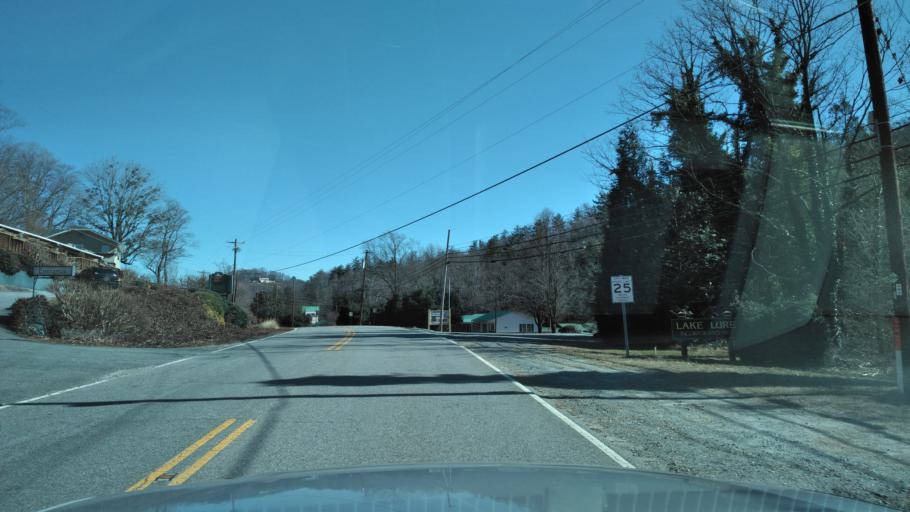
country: US
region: North Carolina
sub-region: Rutherford County
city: Lake Lure
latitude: 35.4375
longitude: -82.2398
